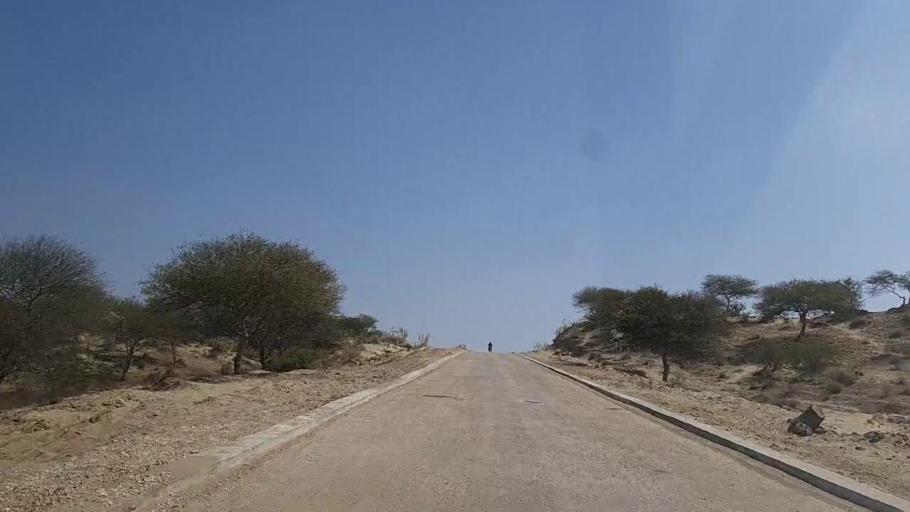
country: PK
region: Sindh
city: Diplo
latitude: 24.4780
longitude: 69.5056
